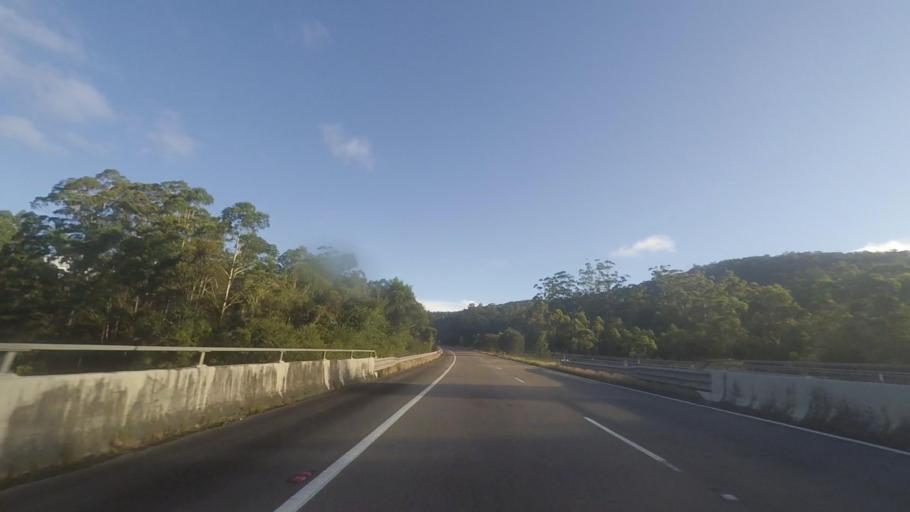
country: AU
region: New South Wales
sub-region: Great Lakes
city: Bulahdelah
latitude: -32.2736
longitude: 152.3288
